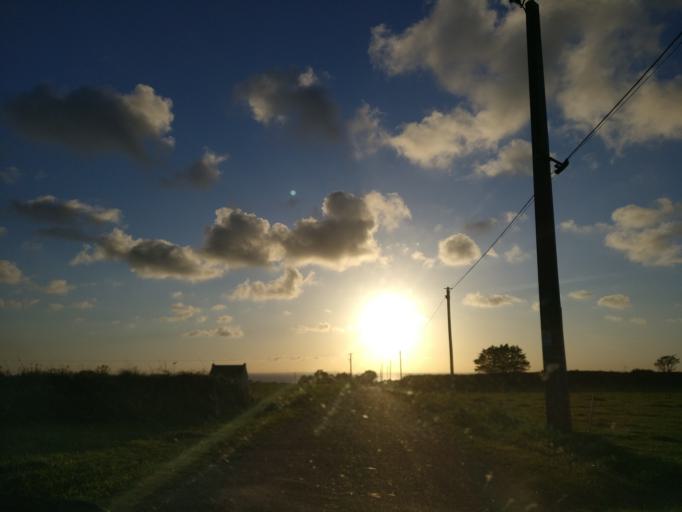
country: FR
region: Brittany
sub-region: Departement du Finistere
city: Lampaul-Plouarzel
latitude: 48.4584
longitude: -4.7471
